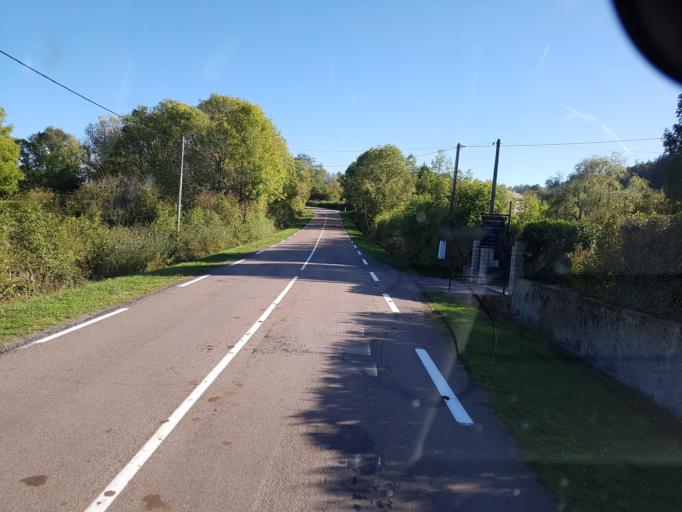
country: FR
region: Bourgogne
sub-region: Departement de Saone-et-Loire
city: Autun
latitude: 47.0575
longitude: 4.2629
